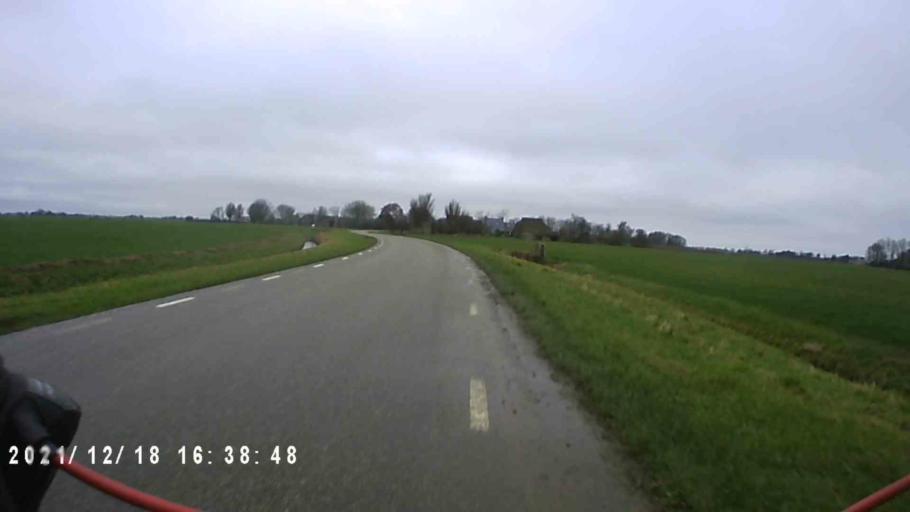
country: NL
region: Friesland
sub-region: Gemeente Dongeradeel
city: Dokkum
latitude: 53.3594
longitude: 6.0098
